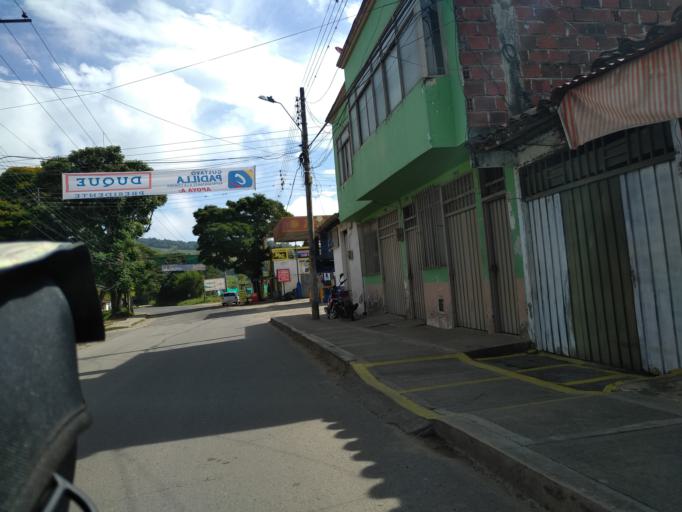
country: CO
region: Valle del Cauca
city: Caicedonia
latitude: 4.3391
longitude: -75.8292
